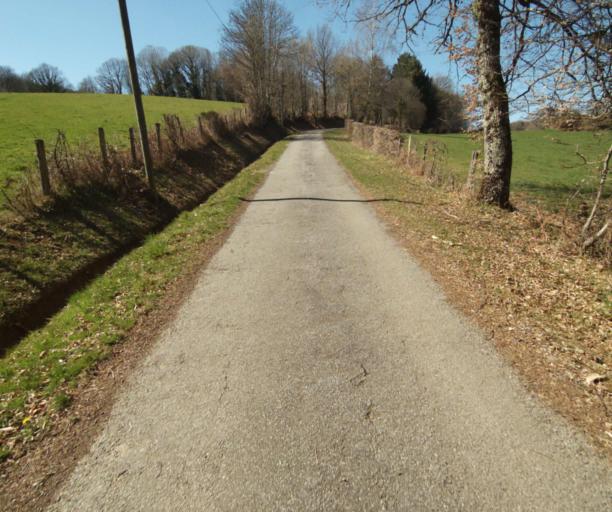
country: FR
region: Limousin
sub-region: Departement de la Correze
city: Chamboulive
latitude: 45.4012
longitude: 1.6719
